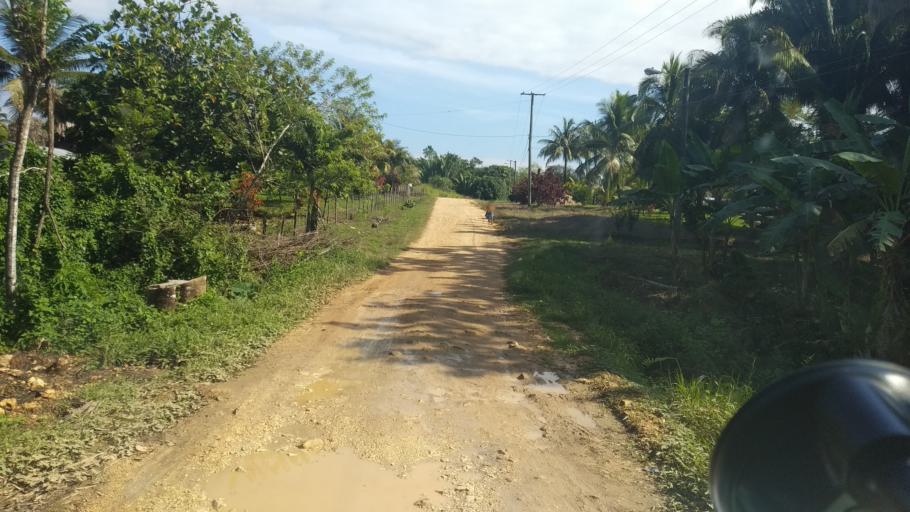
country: BZ
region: Toledo
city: Punta Gorda
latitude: 16.2142
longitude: -88.9093
